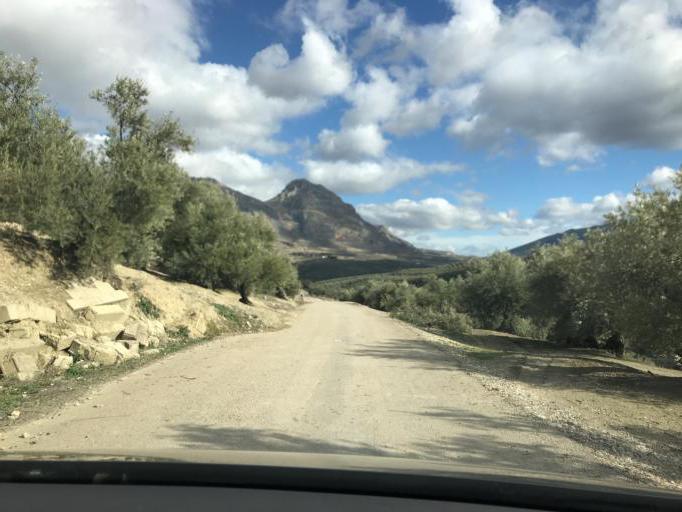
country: ES
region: Andalusia
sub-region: Provincia de Jaen
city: Jimena
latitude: 37.8121
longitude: -3.4479
